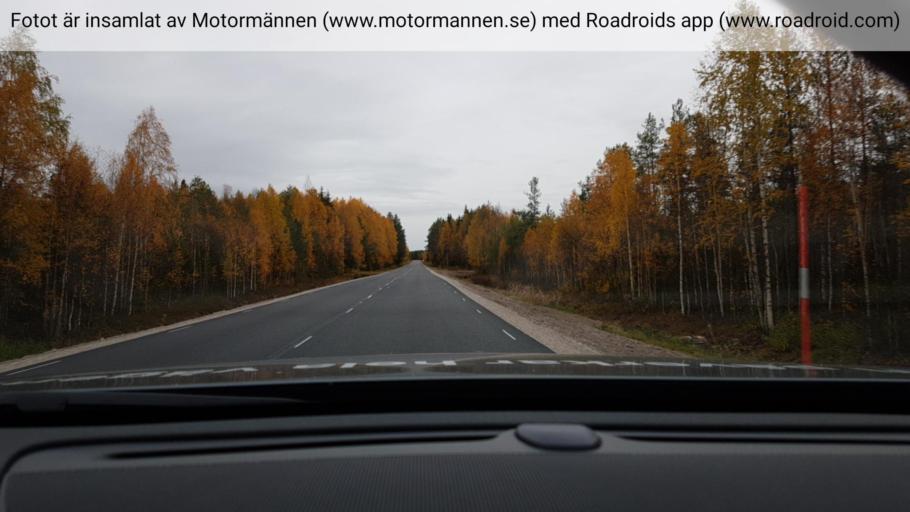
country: SE
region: Norrbotten
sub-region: Overkalix Kommun
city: OEverkalix
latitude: 66.4069
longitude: 22.8061
